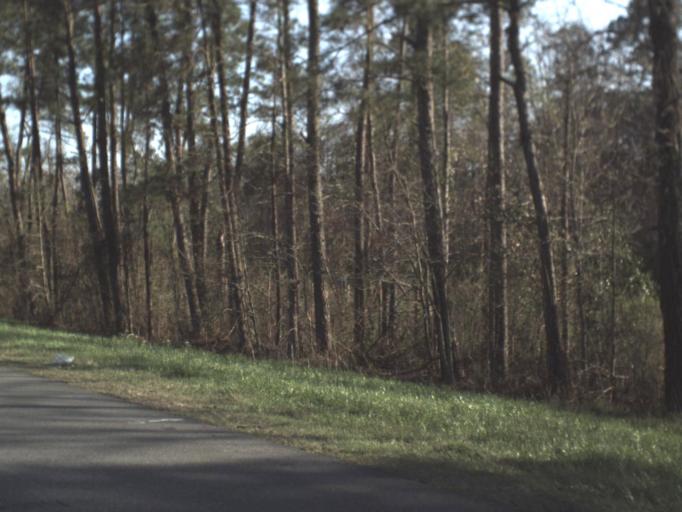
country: US
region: Florida
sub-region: Gadsden County
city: Midway
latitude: 30.4990
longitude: -84.4518
